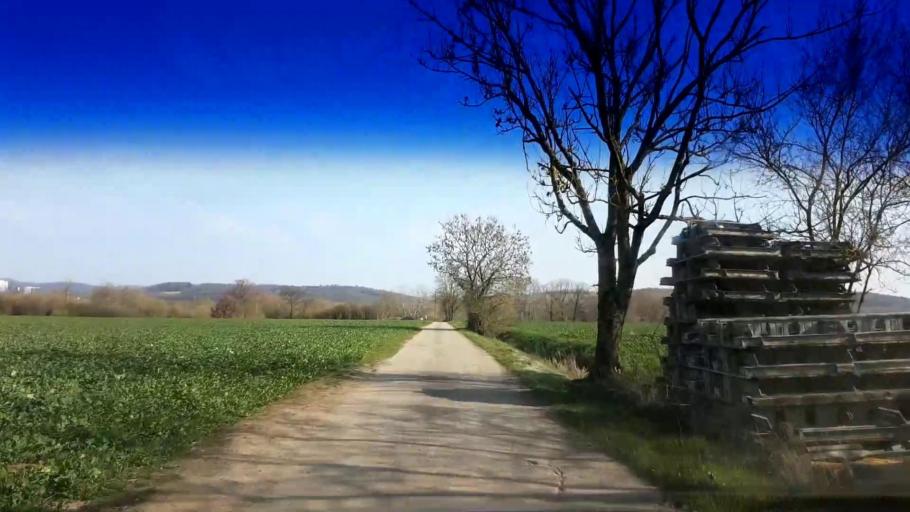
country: DE
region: Bavaria
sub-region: Upper Franconia
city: Ebensfeld
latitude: 50.0506
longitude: 10.9312
